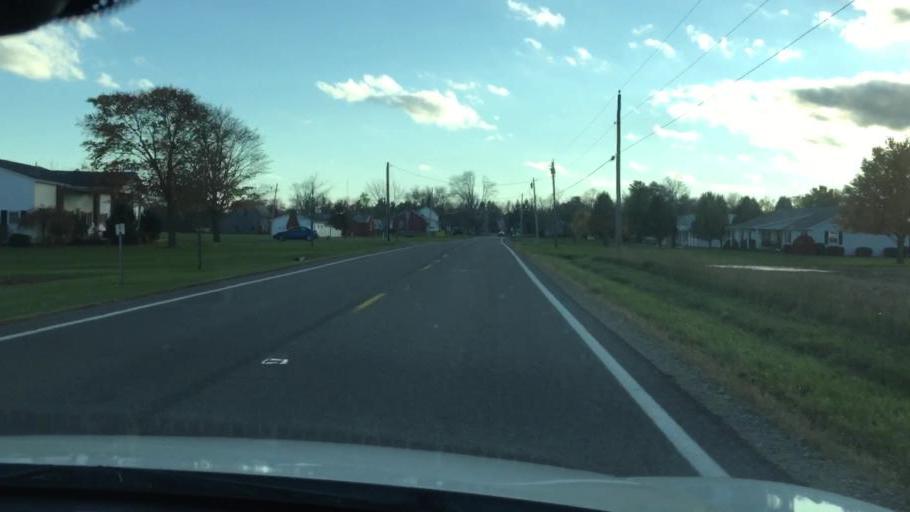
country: US
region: Ohio
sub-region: Champaign County
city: North Lewisburg
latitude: 40.1792
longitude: -83.5248
